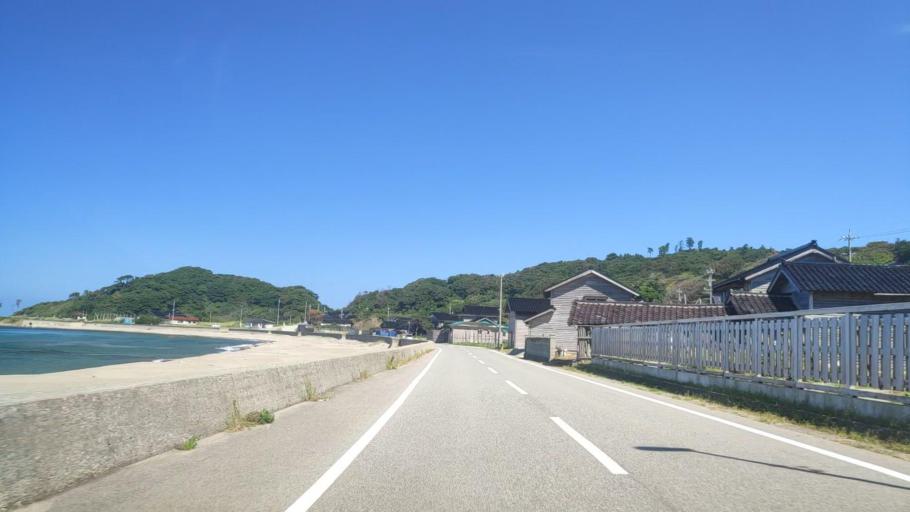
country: JP
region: Ishikawa
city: Nanao
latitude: 37.5094
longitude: 137.2179
